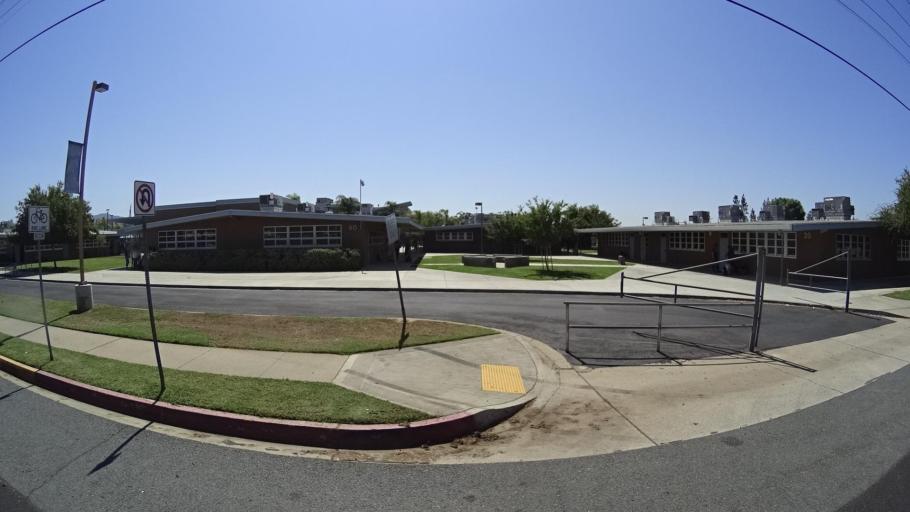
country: US
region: California
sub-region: San Diego County
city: Granite Hills
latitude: 32.8002
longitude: -116.9165
